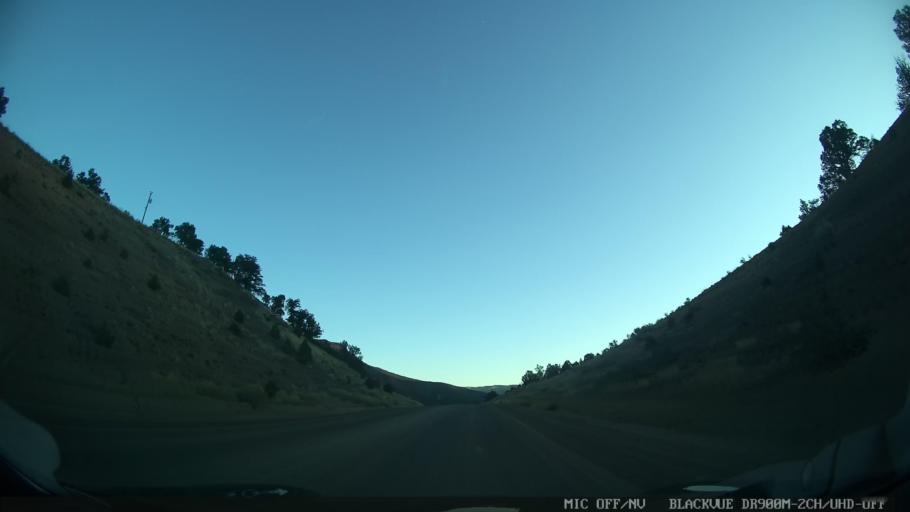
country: US
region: Colorado
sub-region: Eagle County
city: Edwards
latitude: 39.8620
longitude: -106.6431
